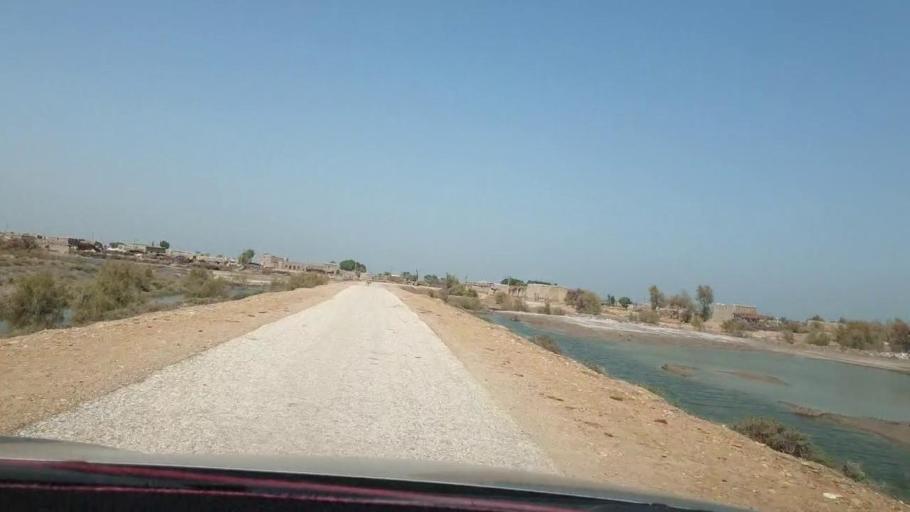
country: PK
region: Sindh
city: Warah
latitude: 27.5748
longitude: 67.7567
